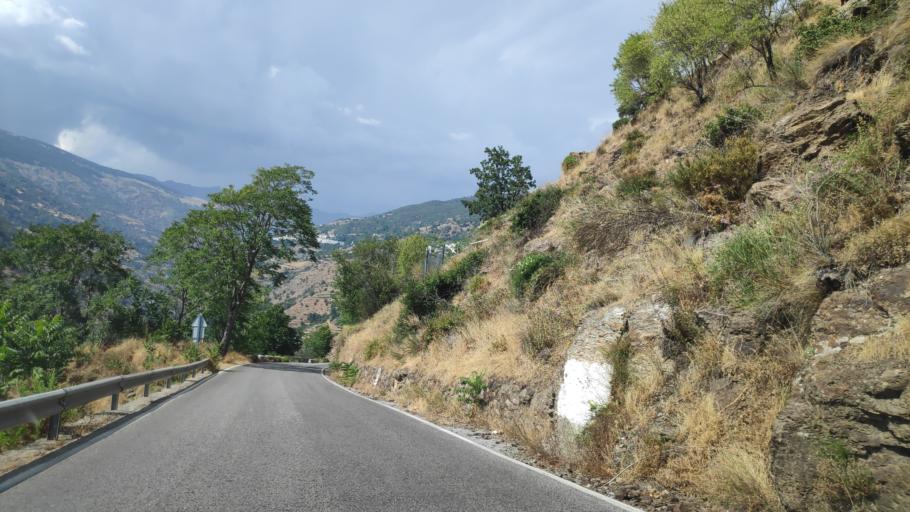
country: ES
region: Andalusia
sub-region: Provincia de Granada
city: Pampaneira
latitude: 36.9351
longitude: -3.3623
